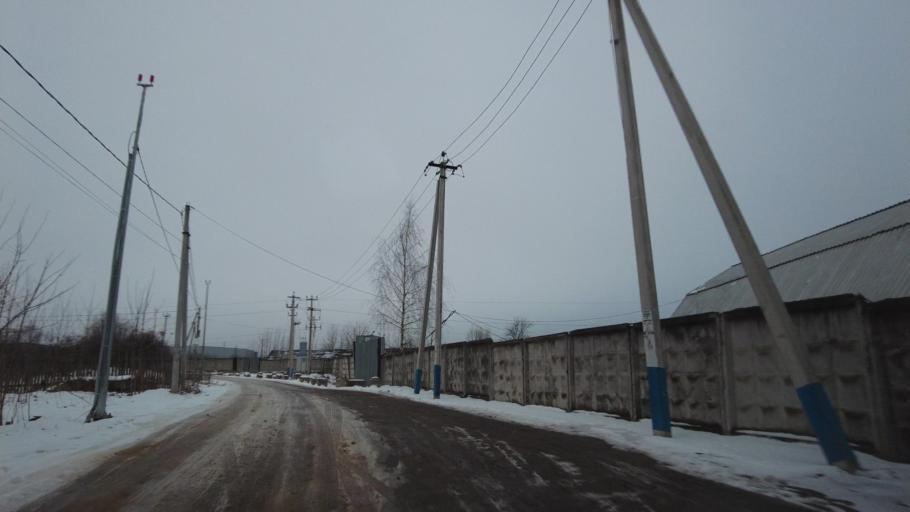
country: RU
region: Moskovskaya
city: Novopodrezkovo
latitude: 55.9913
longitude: 37.3924
